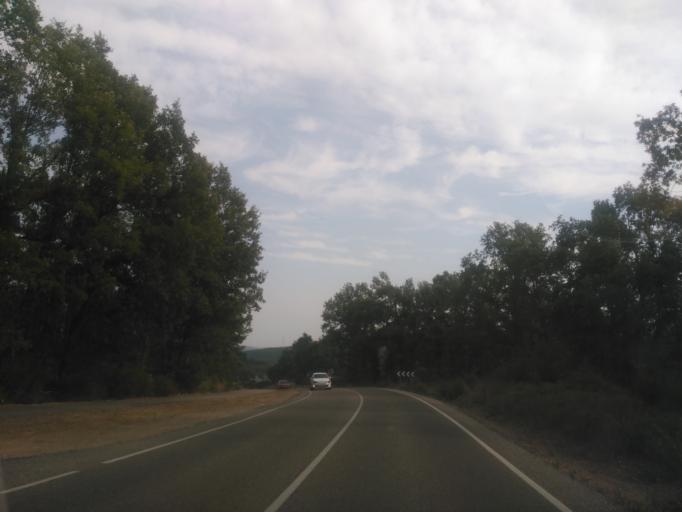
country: ES
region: Castille and Leon
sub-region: Provincia de Zamora
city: Galende
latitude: 42.0860
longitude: -6.6455
